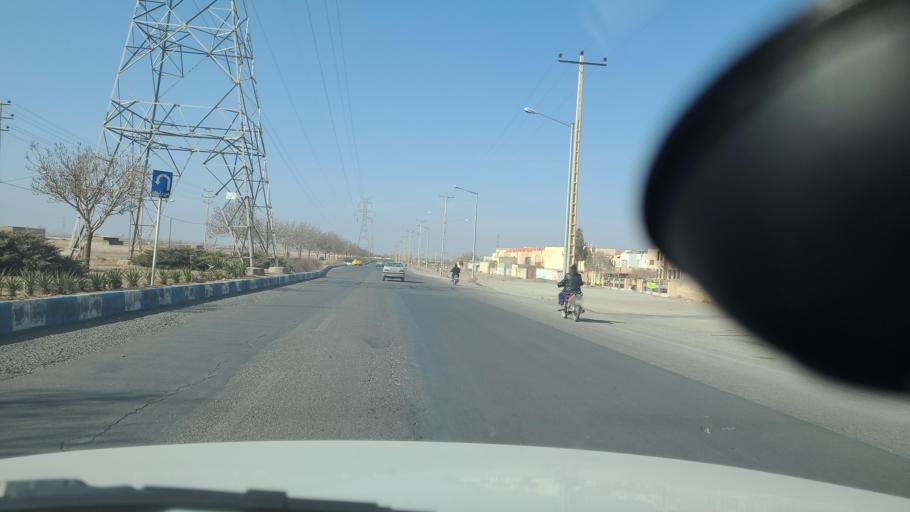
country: IR
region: Razavi Khorasan
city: Fariman
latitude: 35.6965
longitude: 59.8413
